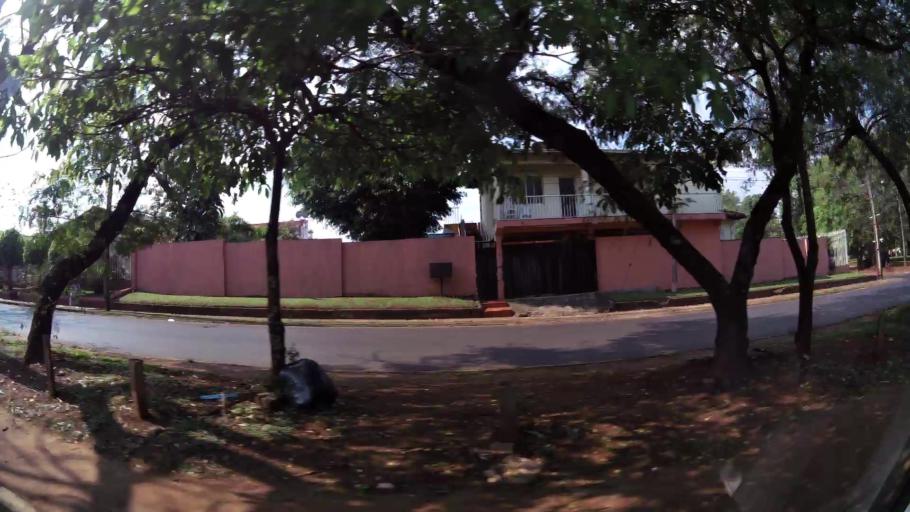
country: PY
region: Alto Parana
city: Presidente Franco
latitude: -25.5358
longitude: -54.6273
